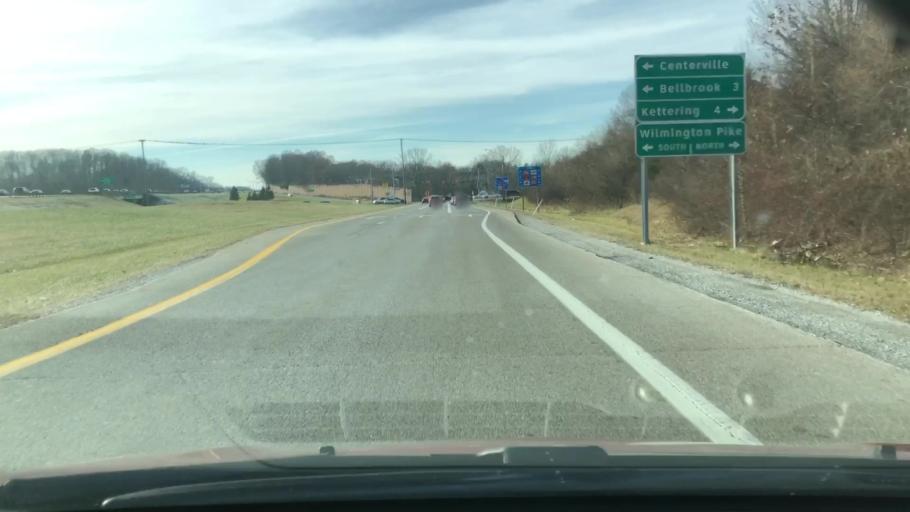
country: US
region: Ohio
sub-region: Greene County
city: Bellbrook
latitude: 39.6571
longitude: -84.1070
